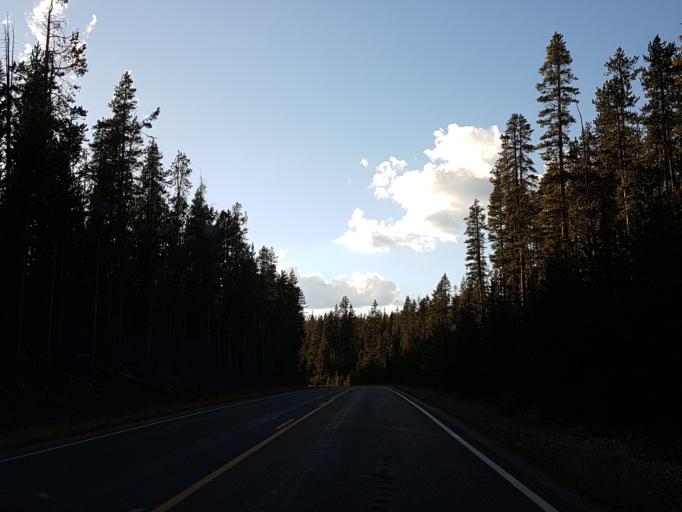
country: US
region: Montana
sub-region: Gallatin County
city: West Yellowstone
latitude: 44.4313
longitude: -110.7552
